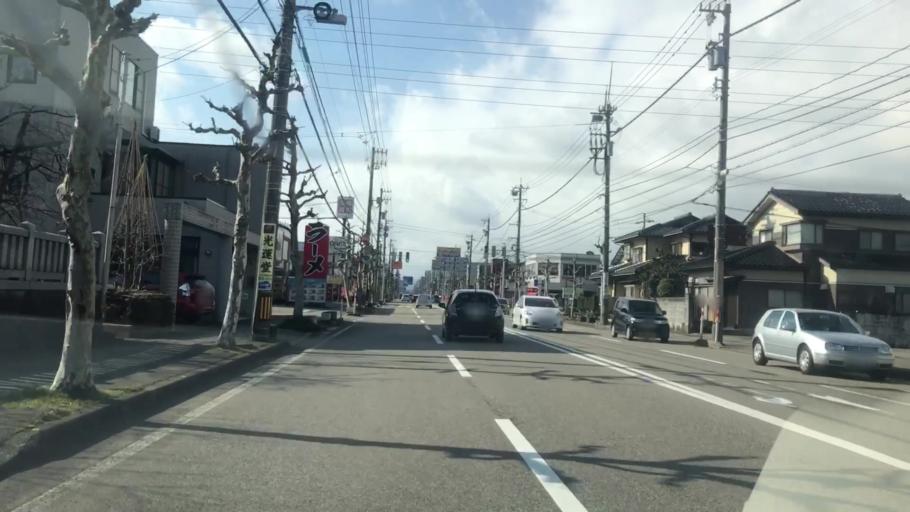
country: JP
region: Toyama
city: Takaoka
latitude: 36.7387
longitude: 137.0251
